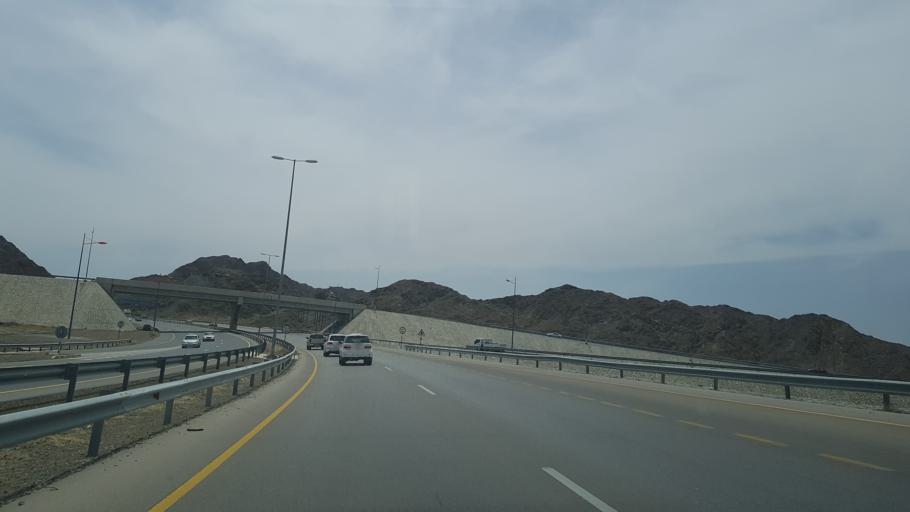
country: OM
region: Muhafazat ad Dakhiliyah
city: Izki
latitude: 22.9731
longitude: 57.7802
